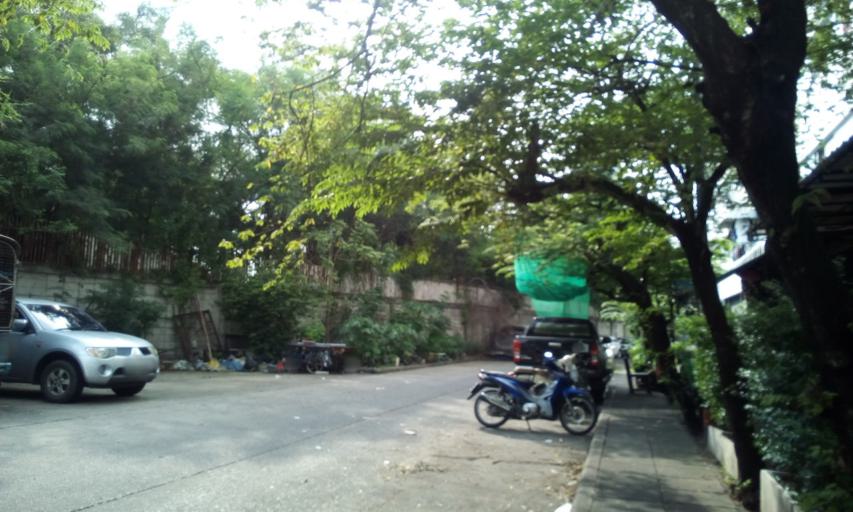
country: TH
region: Bangkok
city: Don Mueang
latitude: 13.9163
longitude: 100.5552
